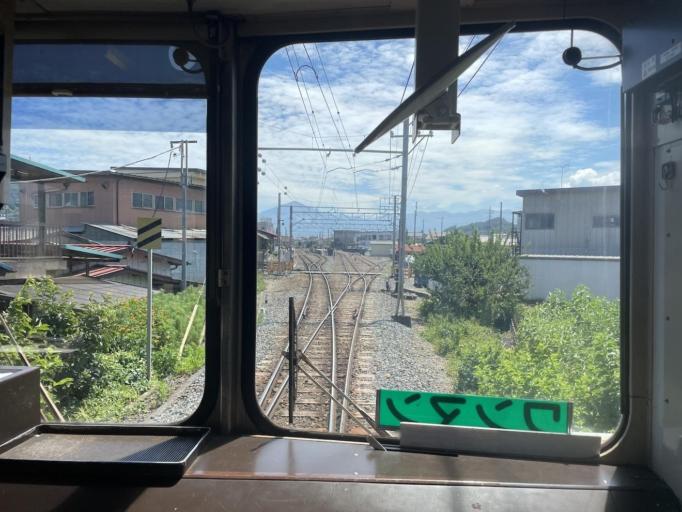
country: JP
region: Saitama
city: Chichibu
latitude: 36.0703
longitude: 139.0940
